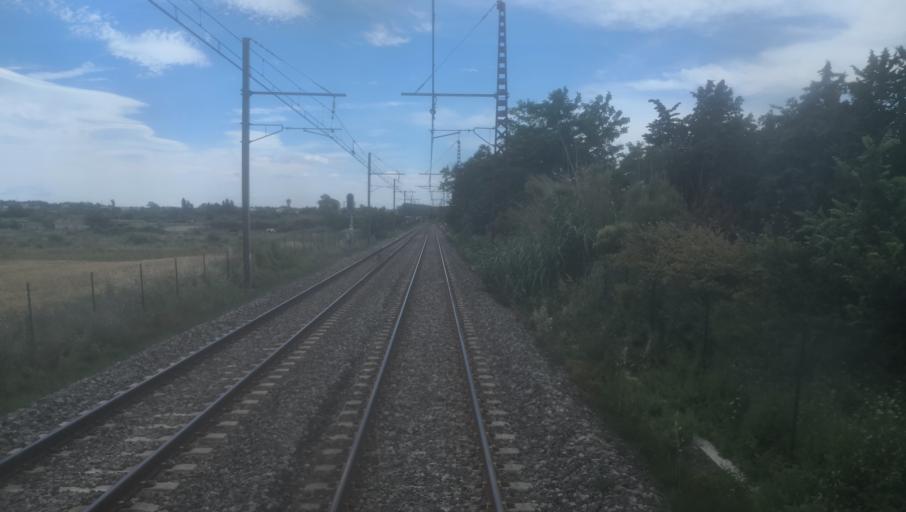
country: FR
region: Languedoc-Roussillon
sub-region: Departement de l'Herault
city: Colombiers
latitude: 43.3254
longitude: 3.1532
